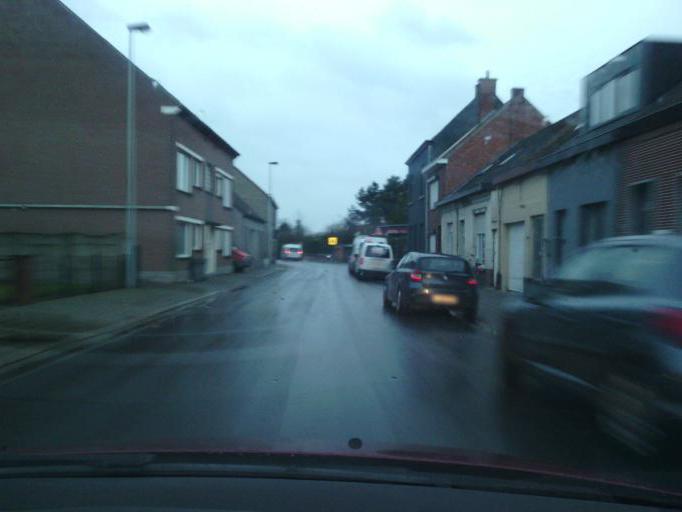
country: BE
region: Flanders
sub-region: Provincie Oost-Vlaanderen
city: Lokeren
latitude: 51.0933
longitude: 3.9935
